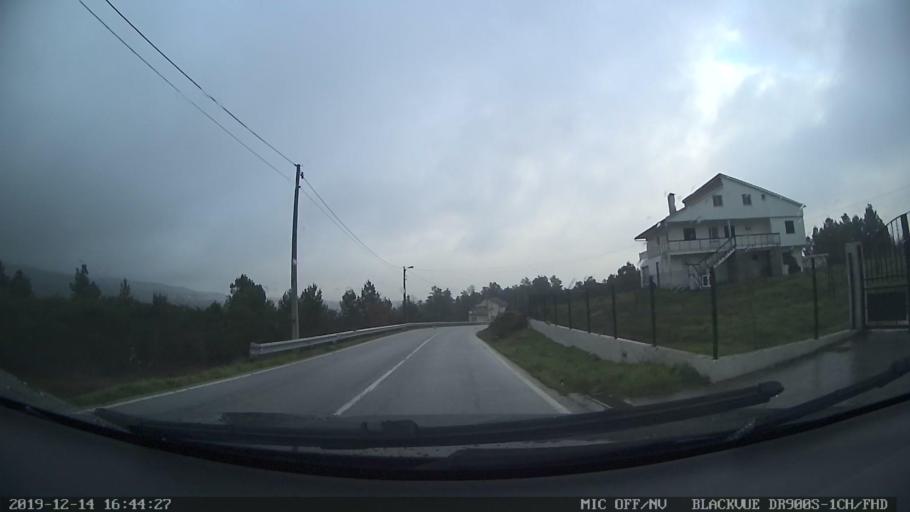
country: PT
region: Vila Real
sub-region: Murca
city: Murca
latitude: 41.3916
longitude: -7.4950
